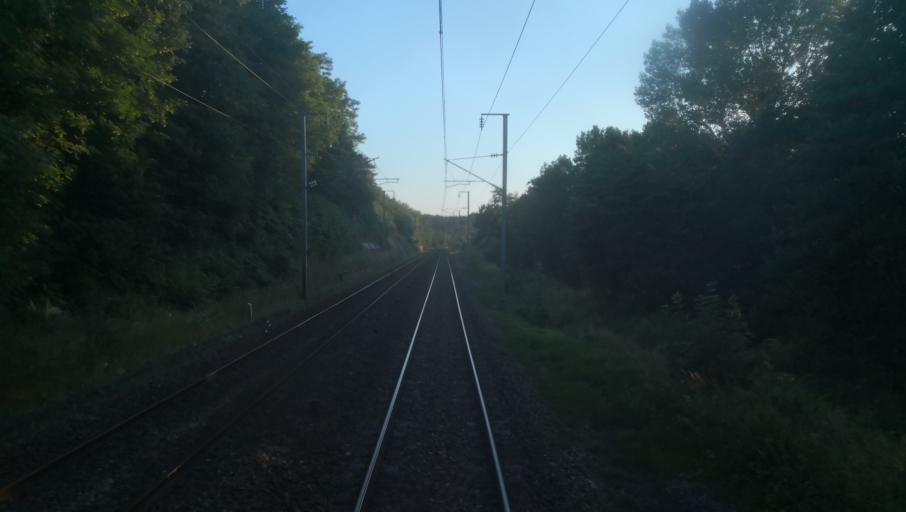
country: FR
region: Haute-Normandie
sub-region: Departement de l'Eure
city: Claville
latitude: 48.9805
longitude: 1.0183
